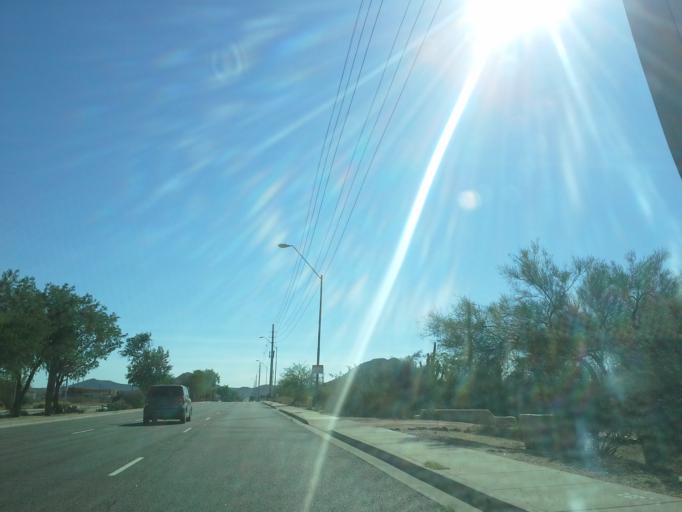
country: US
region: Arizona
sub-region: Maricopa County
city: Scottsdale
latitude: 33.5824
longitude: -111.8212
